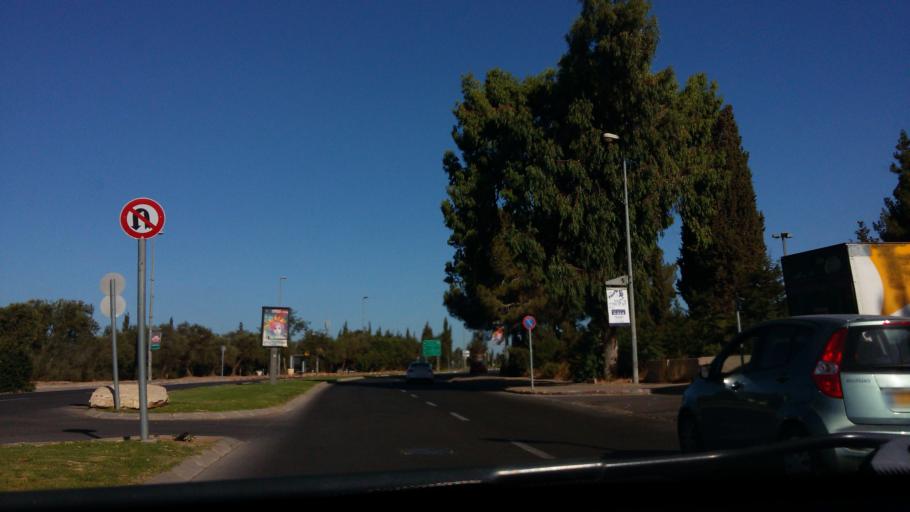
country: IL
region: Jerusalem
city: Jerusalem
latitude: 31.7743
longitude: 35.2061
